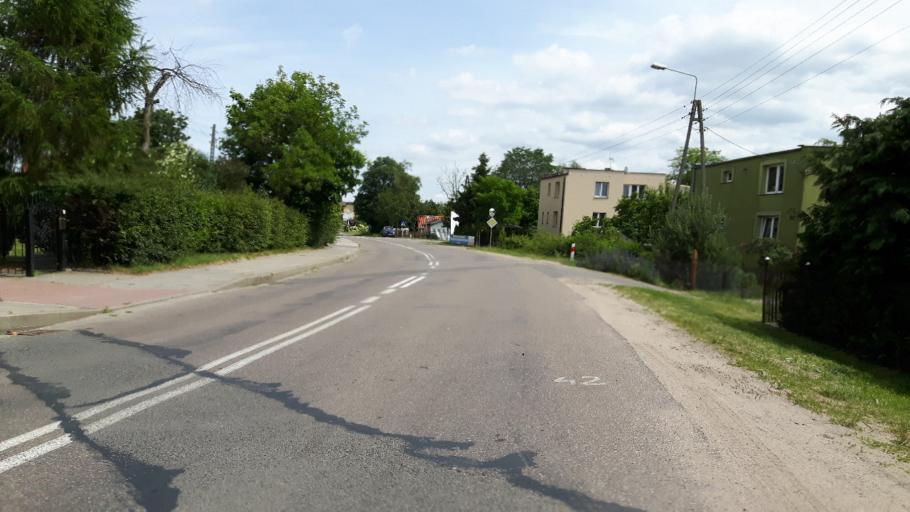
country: PL
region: Pomeranian Voivodeship
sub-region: Powiat nowodworski
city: Stegna
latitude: 54.3272
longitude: 19.1062
